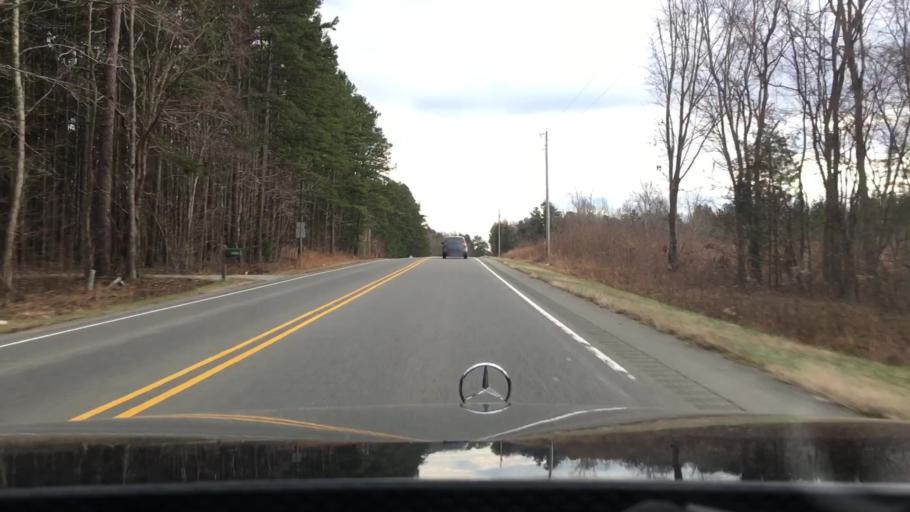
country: US
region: North Carolina
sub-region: Alamance County
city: Mebane
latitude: 36.2374
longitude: -79.1895
